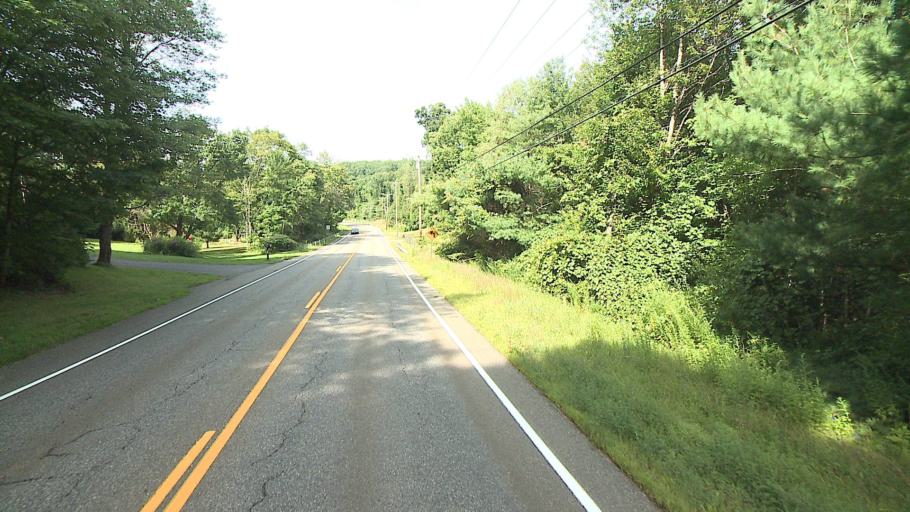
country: US
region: Connecticut
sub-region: Litchfield County
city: Northwest Harwinton
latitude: 41.7651
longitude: -73.1046
